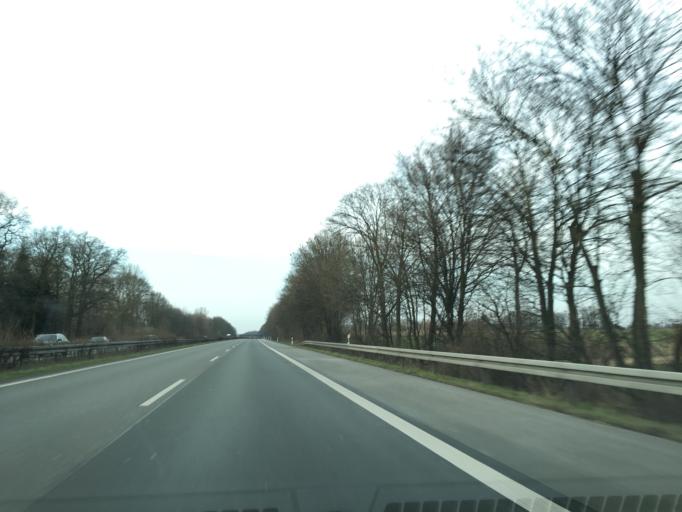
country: DE
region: North Rhine-Westphalia
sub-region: Regierungsbezirk Munster
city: Ascheberg
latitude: 51.7322
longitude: 7.6518
